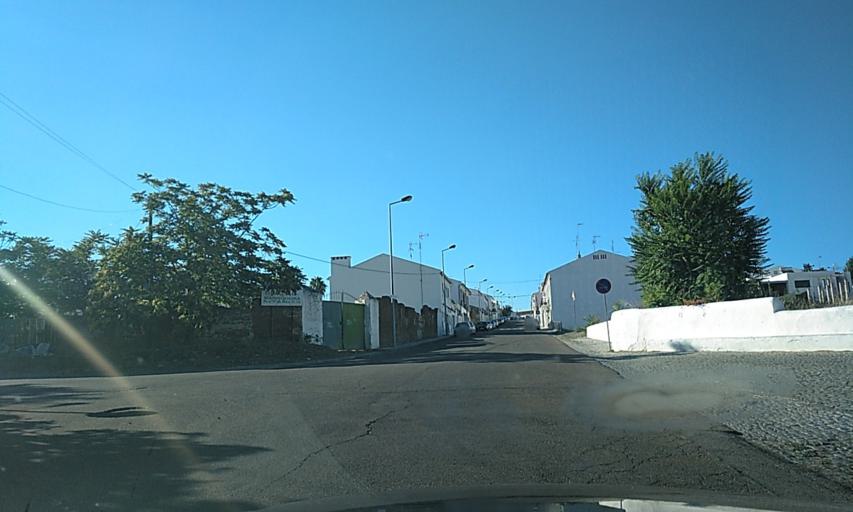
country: PT
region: Portalegre
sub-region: Campo Maior
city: Campo Maior
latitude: 39.0106
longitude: -7.0639
